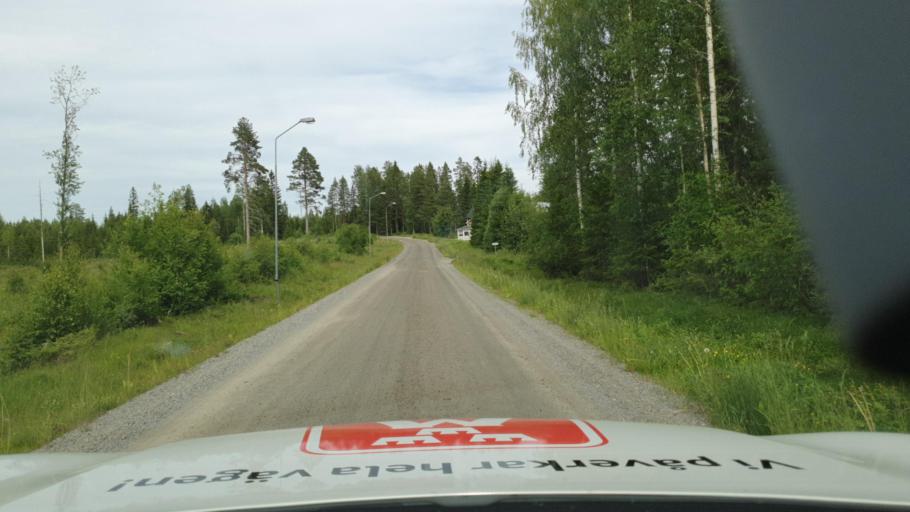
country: SE
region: Vaesterbotten
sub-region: Skelleftea Kommun
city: Viken
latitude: 64.5013
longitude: 20.9249
